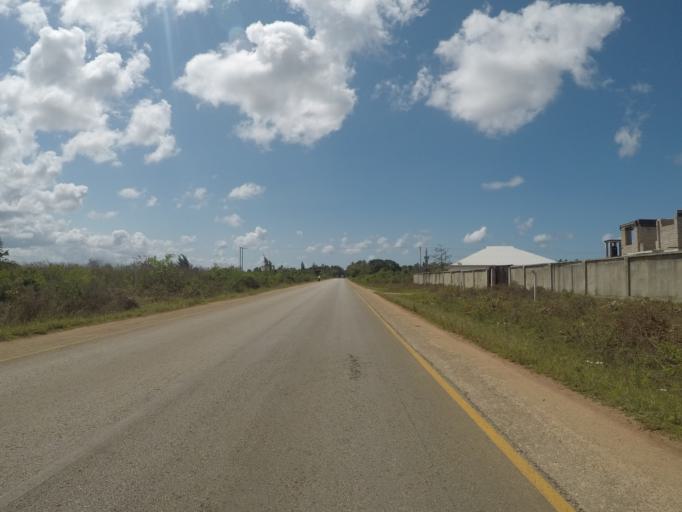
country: TZ
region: Zanzibar Central/South
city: Koani
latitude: -6.1624
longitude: 39.3300
